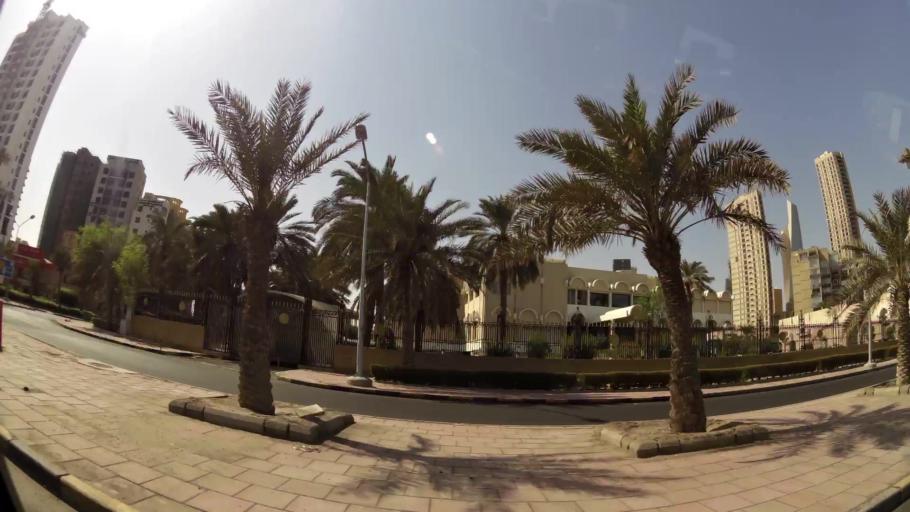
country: KW
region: Al Asimah
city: Ad Dasmah
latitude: 29.3755
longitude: 48.0047
